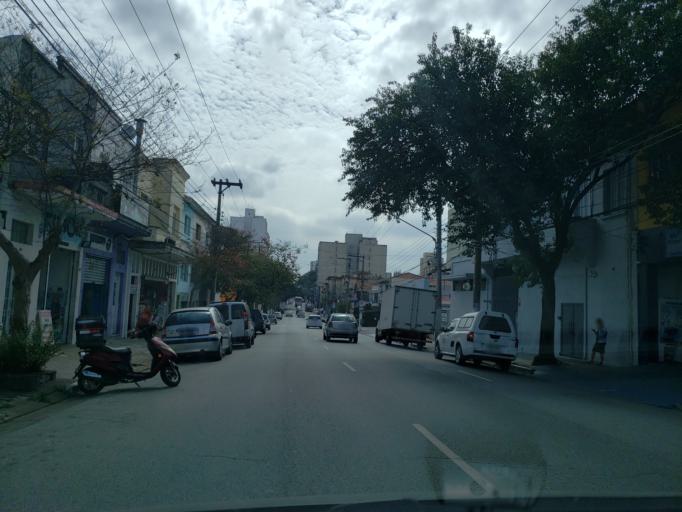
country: BR
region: Sao Paulo
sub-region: Sao Paulo
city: Sao Paulo
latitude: -23.5881
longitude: -46.6073
